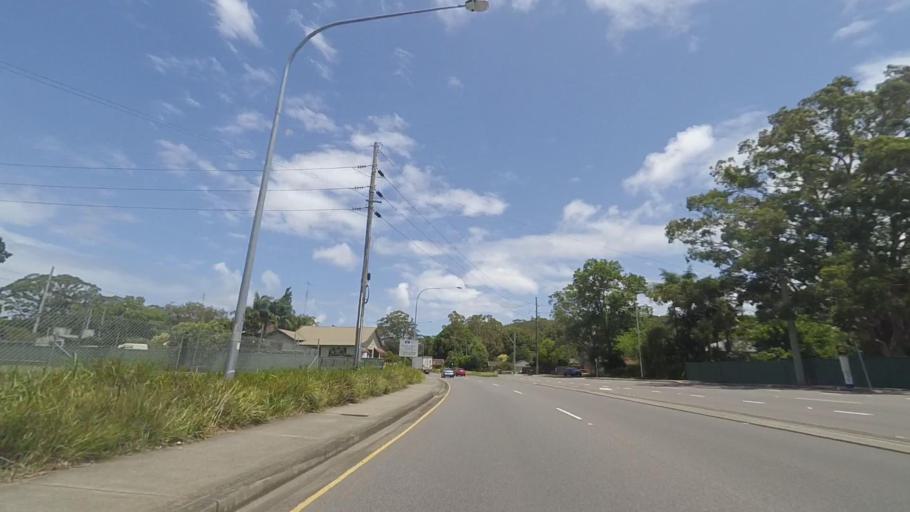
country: AU
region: New South Wales
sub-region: Gosford Shire
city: Lisarow
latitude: -33.3495
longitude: 151.3694
